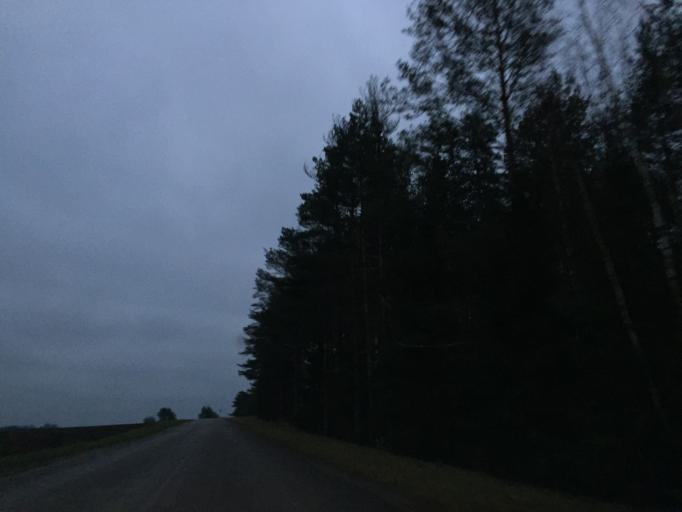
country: LV
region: Koceni
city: Koceni
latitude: 57.5510
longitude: 25.2396
